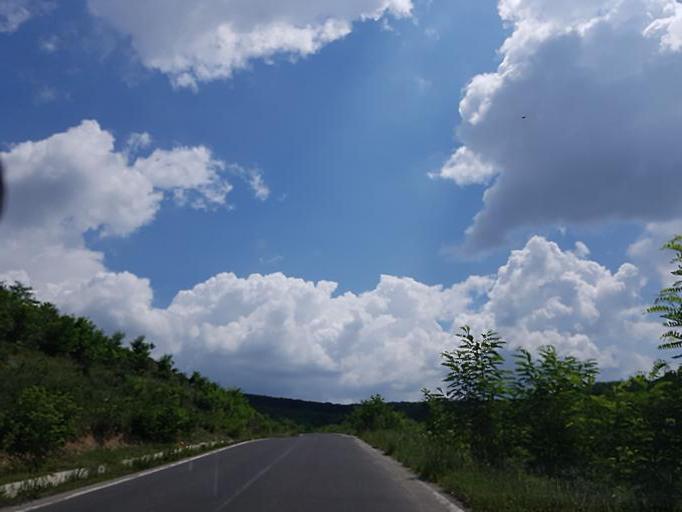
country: RO
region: Sibiu
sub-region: Comuna Seica Mica
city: Seica Mica
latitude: 46.0486
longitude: 24.1480
